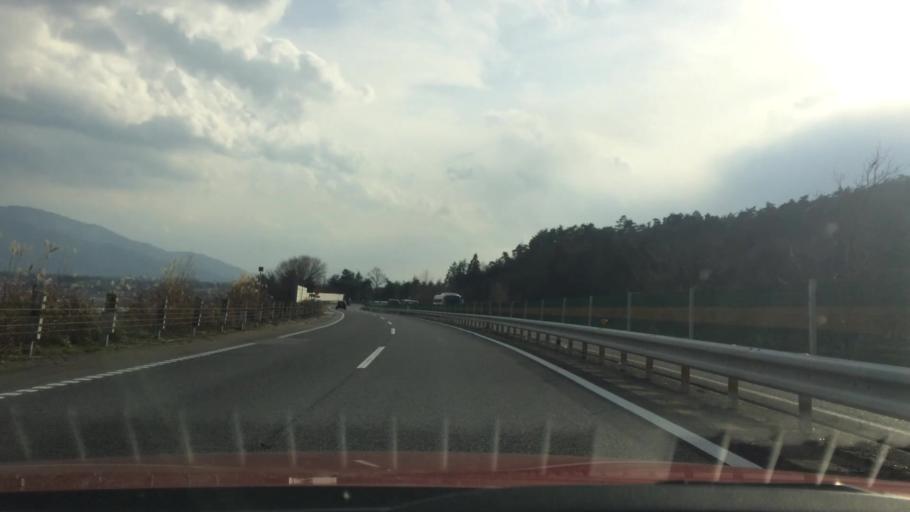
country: JP
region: Nagano
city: Ina
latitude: 35.7796
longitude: 137.9328
